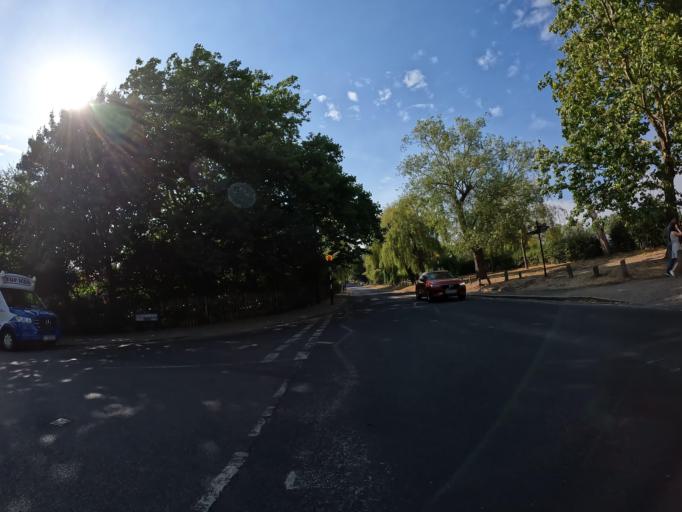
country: GB
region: England
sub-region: Hertfordshire
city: Potters Bar
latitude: 51.6845
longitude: -0.1607
